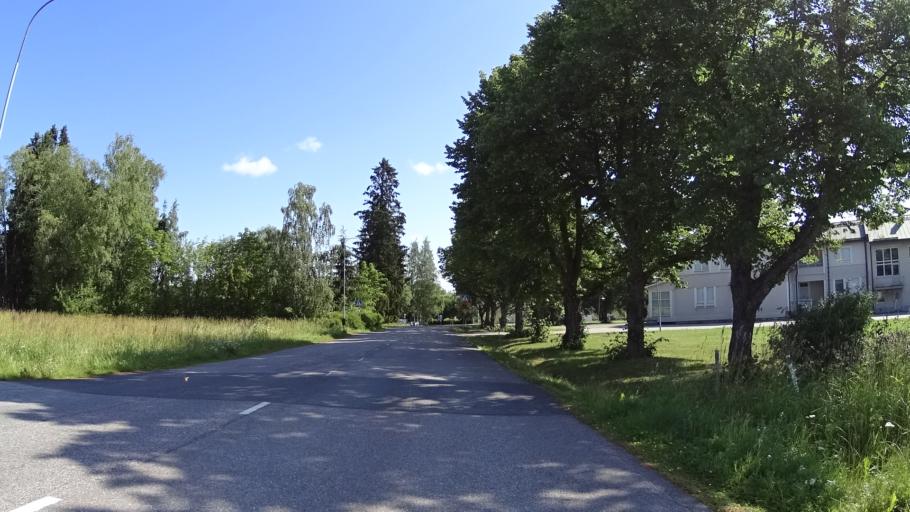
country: FI
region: Uusimaa
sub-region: Helsinki
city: Tuusula
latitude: 60.4148
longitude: 25.0476
